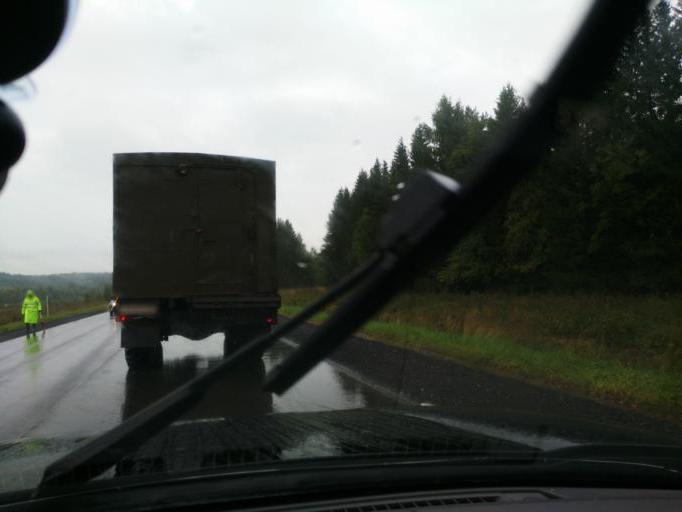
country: RU
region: Perm
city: Yugo-Kamskiy
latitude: 57.4740
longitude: 55.6778
